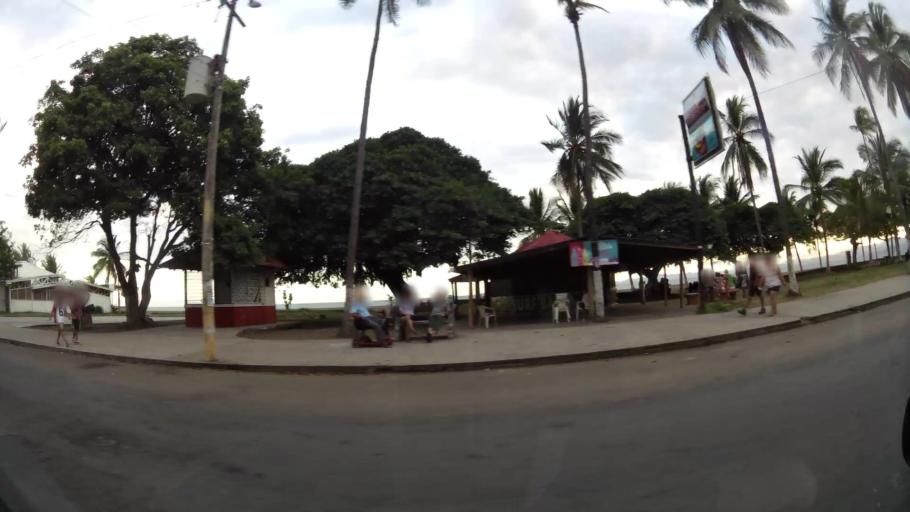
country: CR
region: Puntarenas
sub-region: Canton Central de Puntarenas
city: Puntarenas
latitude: 9.9749
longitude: -84.8384
